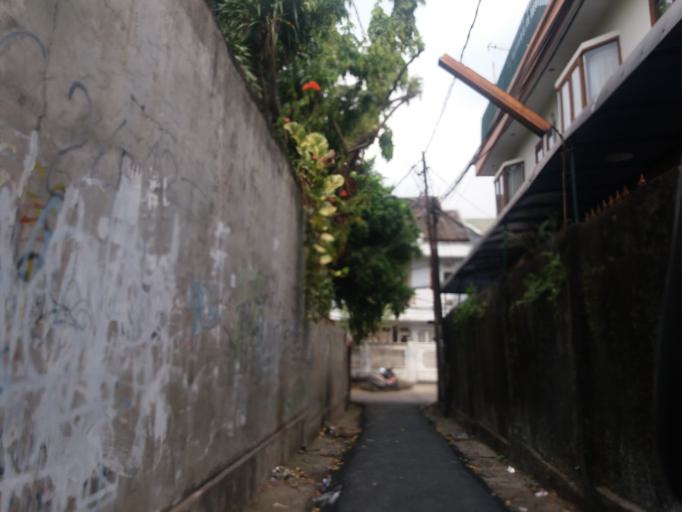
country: ID
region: Jakarta Raya
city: Jakarta
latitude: -6.1903
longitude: 106.8192
